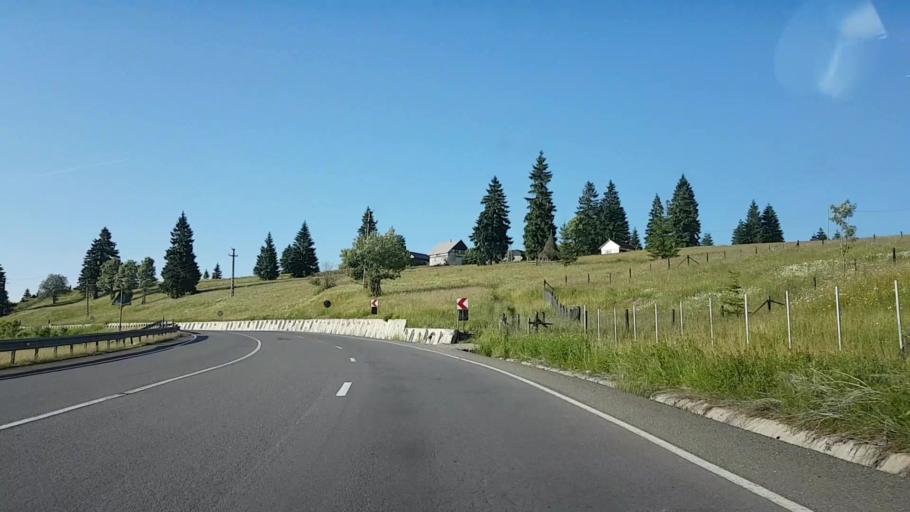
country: RO
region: Bistrita-Nasaud
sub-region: Comuna Lunca Ilvei
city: Lunca Ilvei
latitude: 47.2445
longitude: 25.0209
